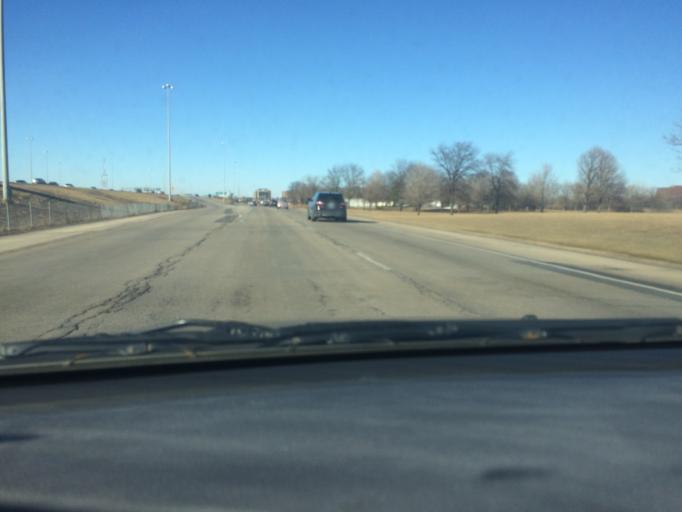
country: US
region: Illinois
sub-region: Cook County
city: Rolling Meadows
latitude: 42.0447
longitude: -88.0292
